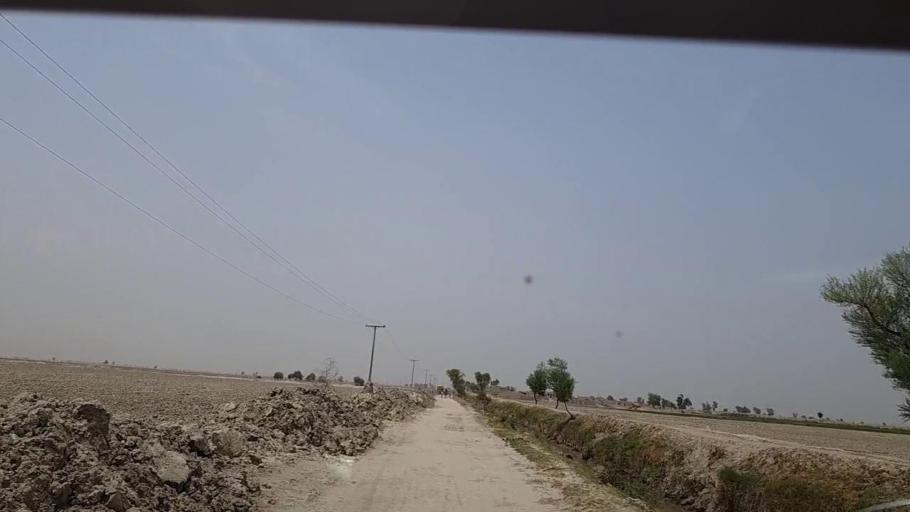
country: PK
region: Sindh
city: Khairpur Nathan Shah
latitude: 27.0498
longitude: 67.6191
